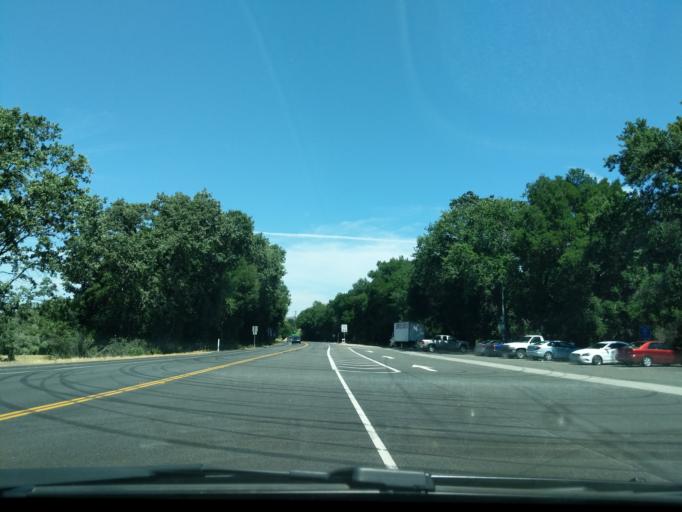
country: US
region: California
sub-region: San Luis Obispo County
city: Santa Margarita
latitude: 35.3834
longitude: -120.6281
